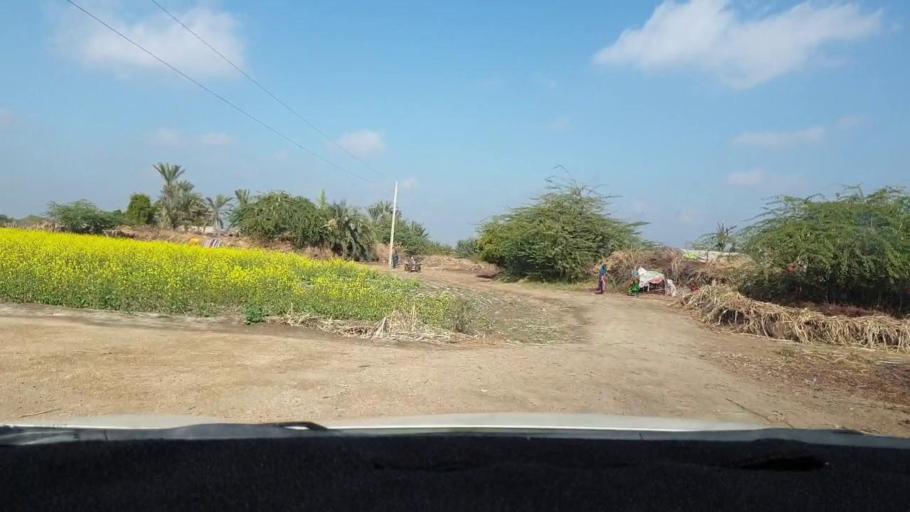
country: PK
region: Sindh
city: Berani
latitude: 25.7232
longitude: 68.9832
